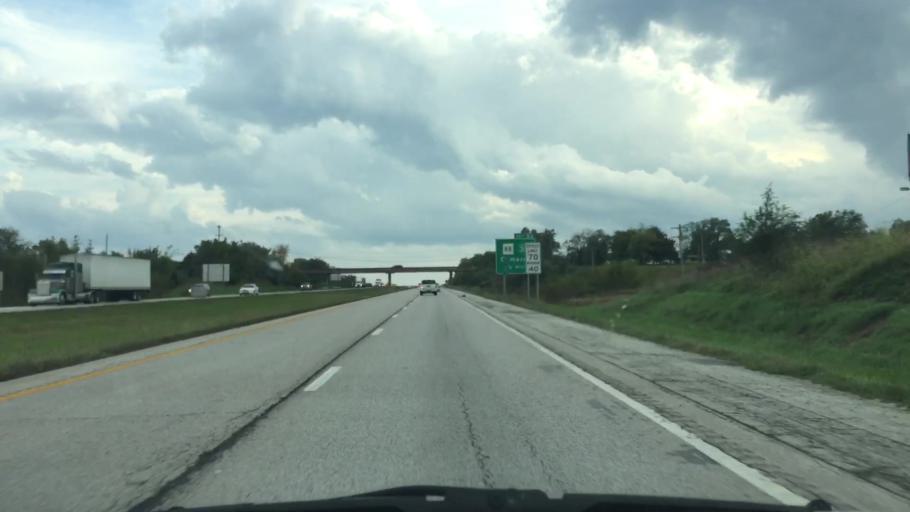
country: US
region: Missouri
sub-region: Clinton County
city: Cameron
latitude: 39.7451
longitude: -94.2203
